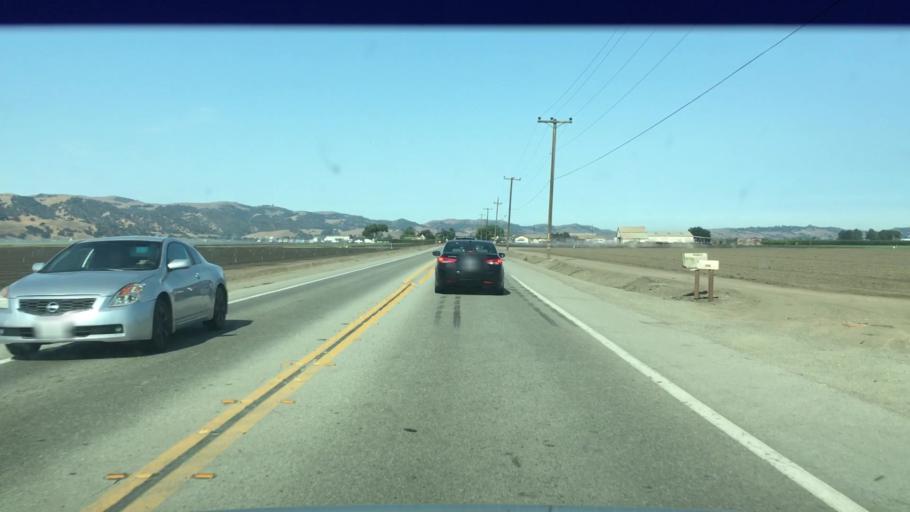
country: US
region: California
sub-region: San Benito County
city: Hollister
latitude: 36.8417
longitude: -121.4655
